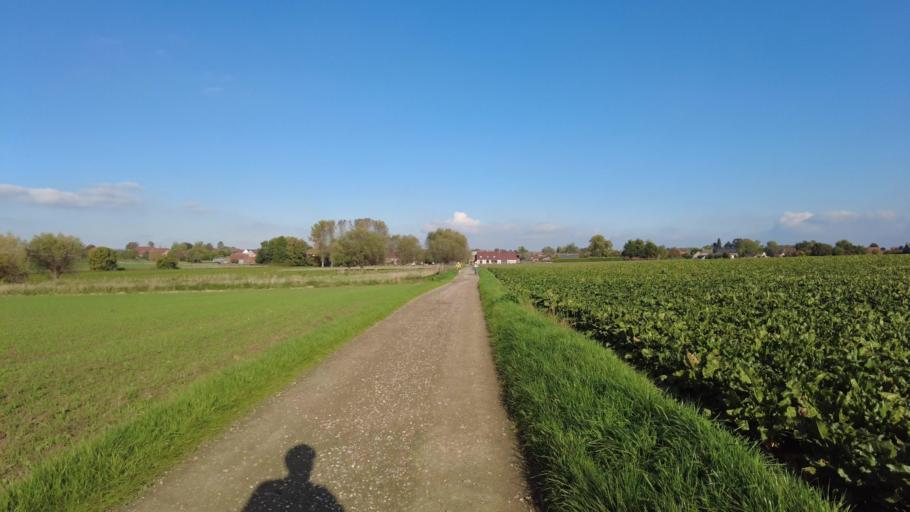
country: BE
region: Wallonia
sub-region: Province du Brabant Wallon
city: Jodoigne
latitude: 50.7351
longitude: 4.8903
